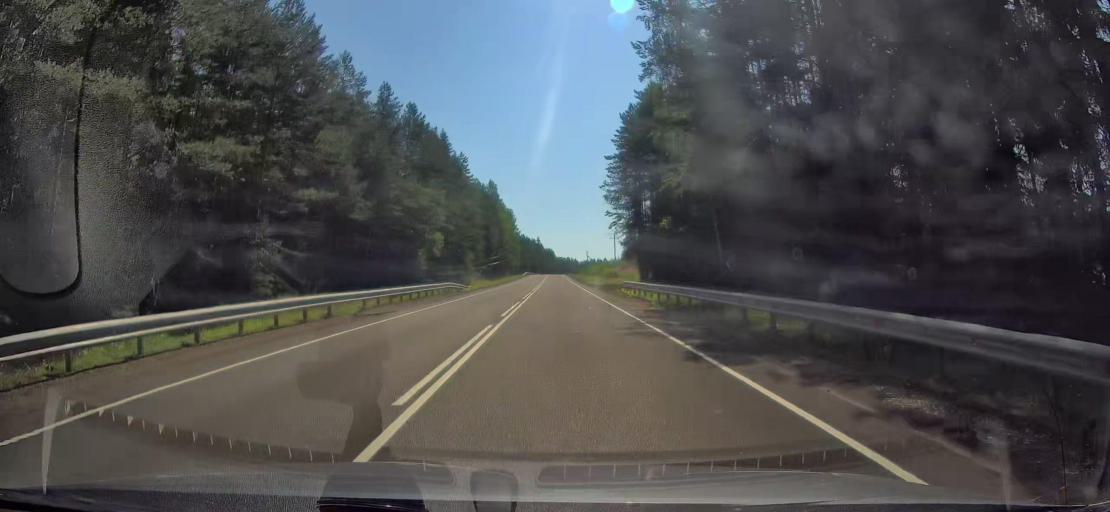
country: RU
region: Leningrad
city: Yefimovskiy
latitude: 59.3844
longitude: 34.7758
